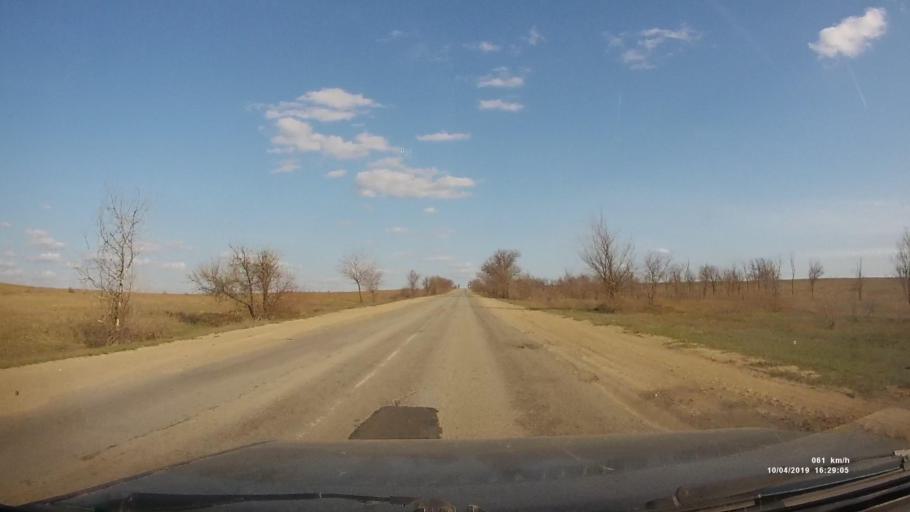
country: RU
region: Rostov
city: Staraya Stanitsa
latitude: 48.2704
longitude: 40.3512
